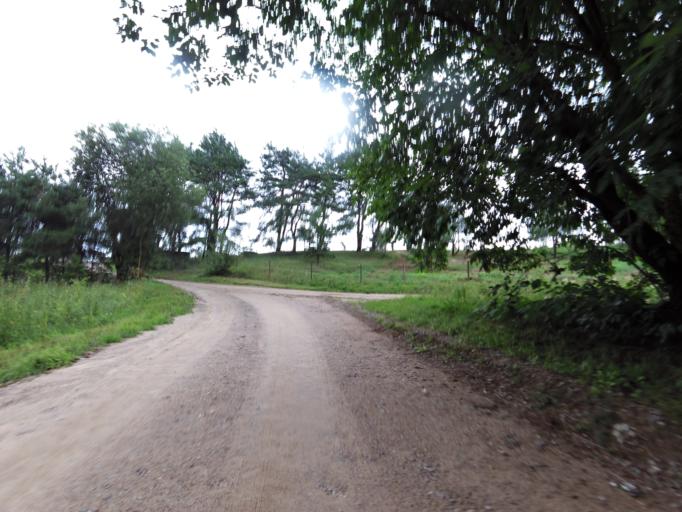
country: LT
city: Grigiskes
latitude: 54.7084
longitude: 25.1015
